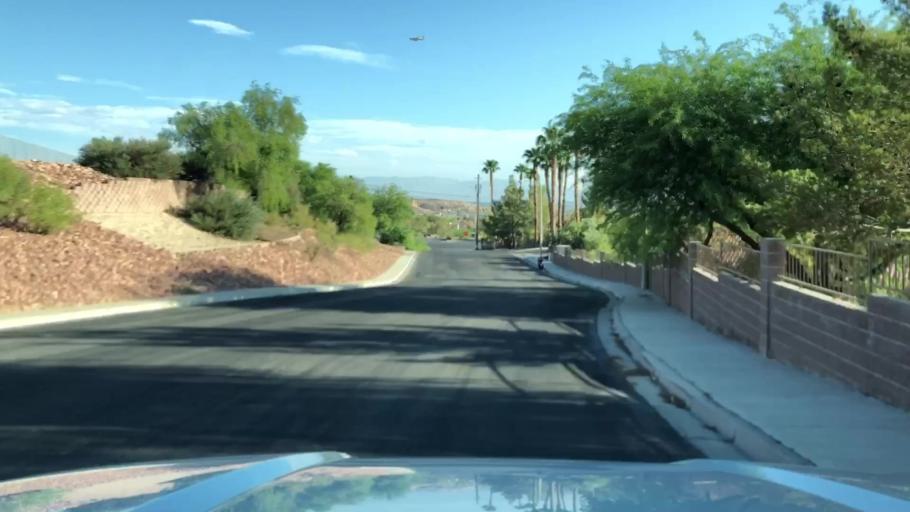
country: US
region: Nevada
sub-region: Clark County
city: Whitney
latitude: 36.0546
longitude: -115.0587
